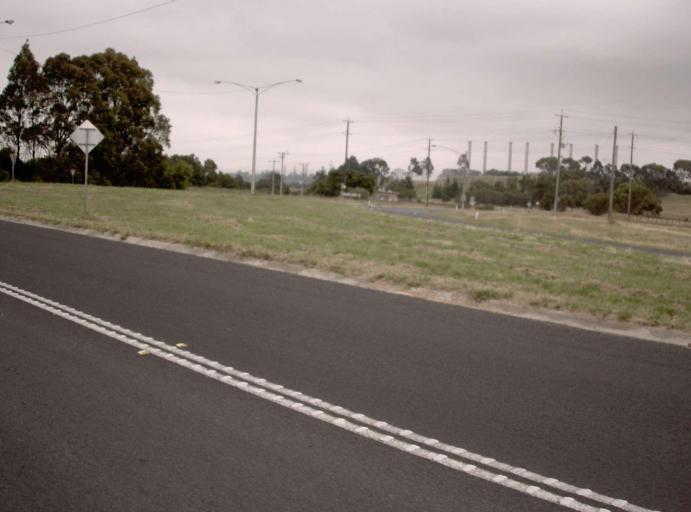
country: AU
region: Victoria
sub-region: Latrobe
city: Morwell
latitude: -38.2789
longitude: 146.4139
